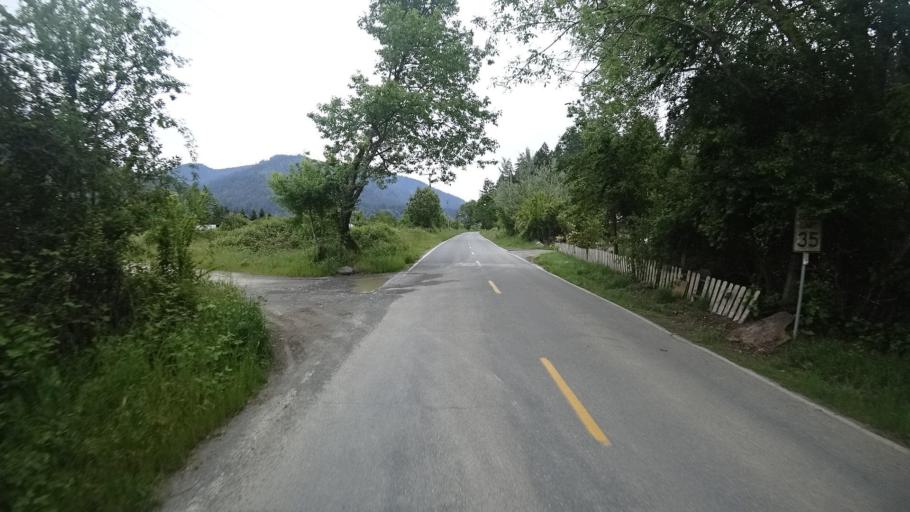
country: US
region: California
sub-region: Humboldt County
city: Willow Creek
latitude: 41.0777
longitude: -123.6972
